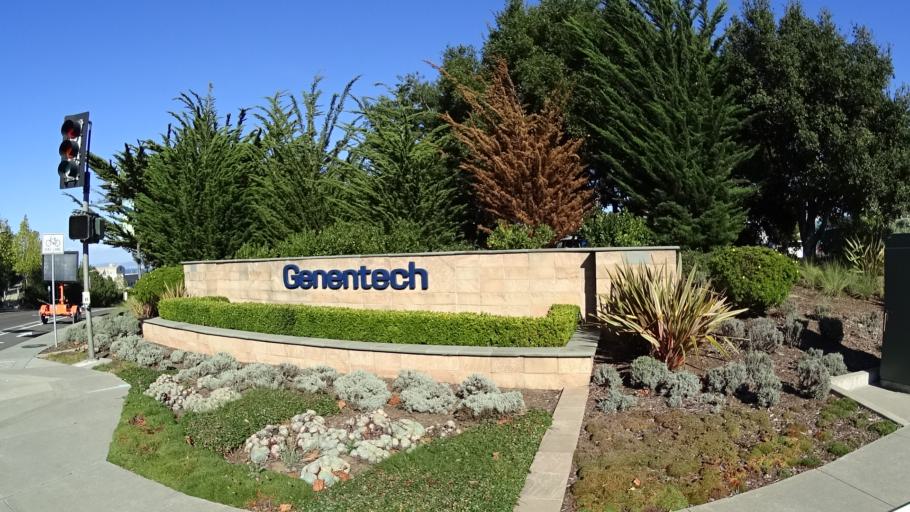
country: US
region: California
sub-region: San Mateo County
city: South San Francisco
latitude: 37.6544
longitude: -122.3806
